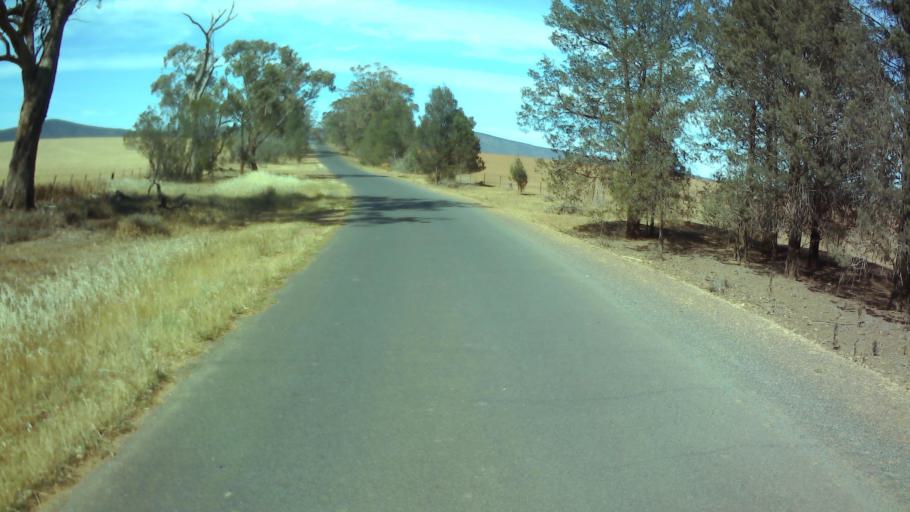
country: AU
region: New South Wales
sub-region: Weddin
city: Grenfell
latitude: -33.9322
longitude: 148.0848
